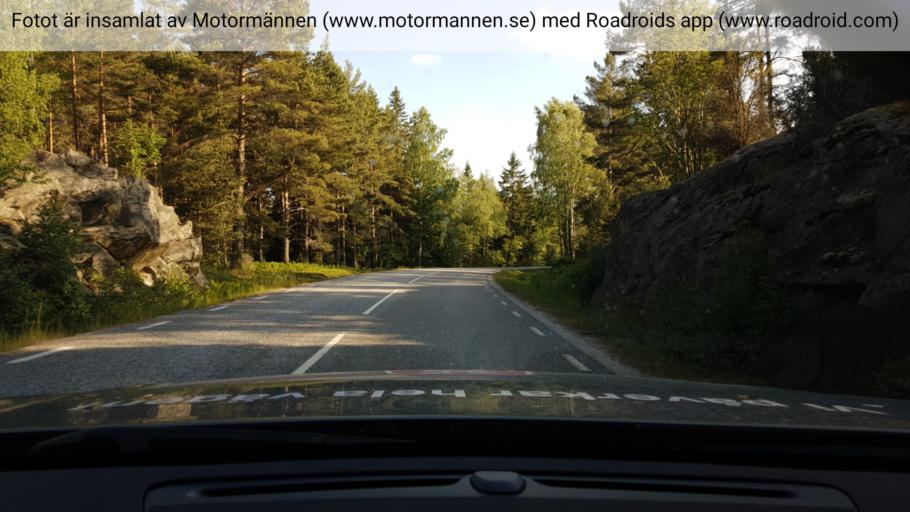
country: SE
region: Stockholm
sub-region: Haninge Kommun
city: Jordbro
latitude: 58.9923
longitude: 18.1004
